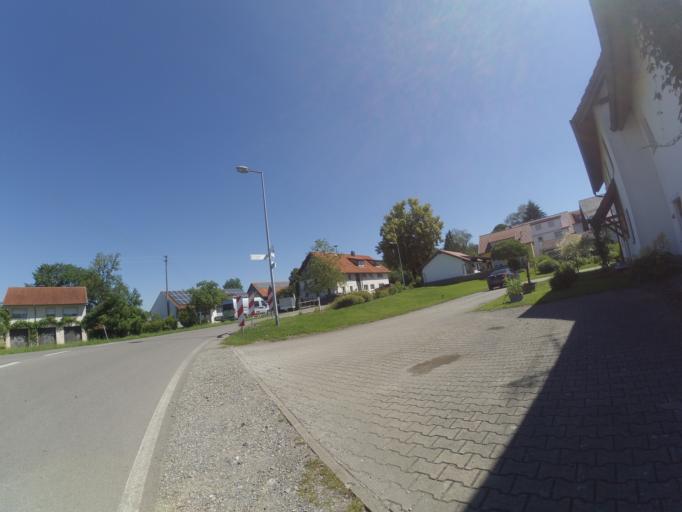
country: DE
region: Baden-Wuerttemberg
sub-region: Tuebingen Region
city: Bad Wurzach
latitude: 47.8668
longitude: 9.9324
